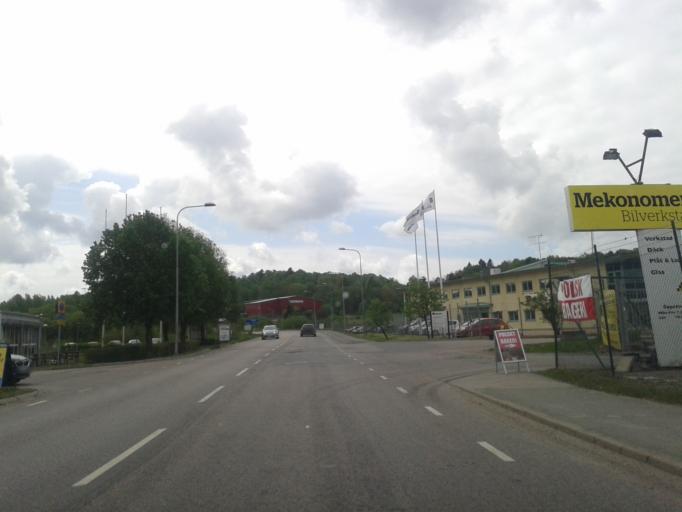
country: SE
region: Vaestra Goetaland
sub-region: Goteborg
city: Hammarkullen
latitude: 57.7911
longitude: 12.0465
